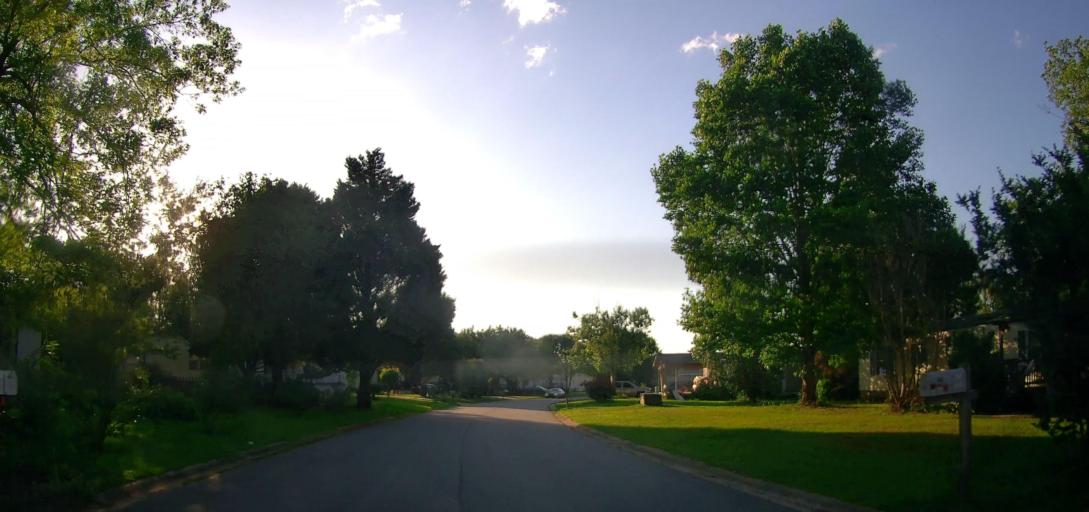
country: US
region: Georgia
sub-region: Houston County
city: Centerville
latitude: 32.6364
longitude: -83.7234
